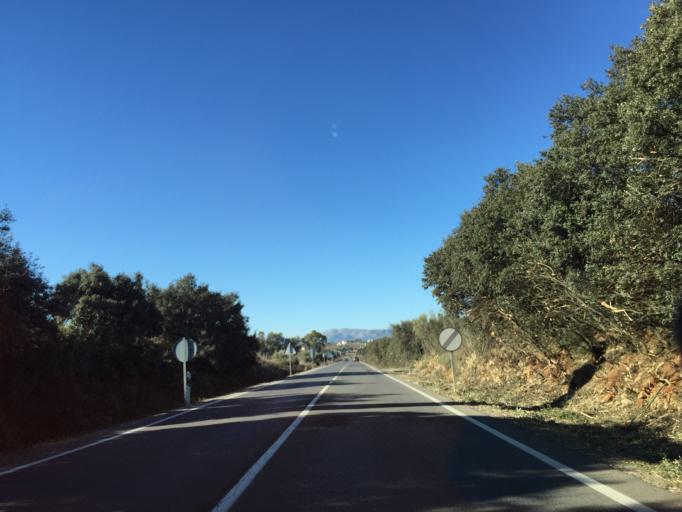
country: ES
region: Andalusia
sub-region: Provincia de Malaga
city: Arriate
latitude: 36.7798
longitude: -5.1198
